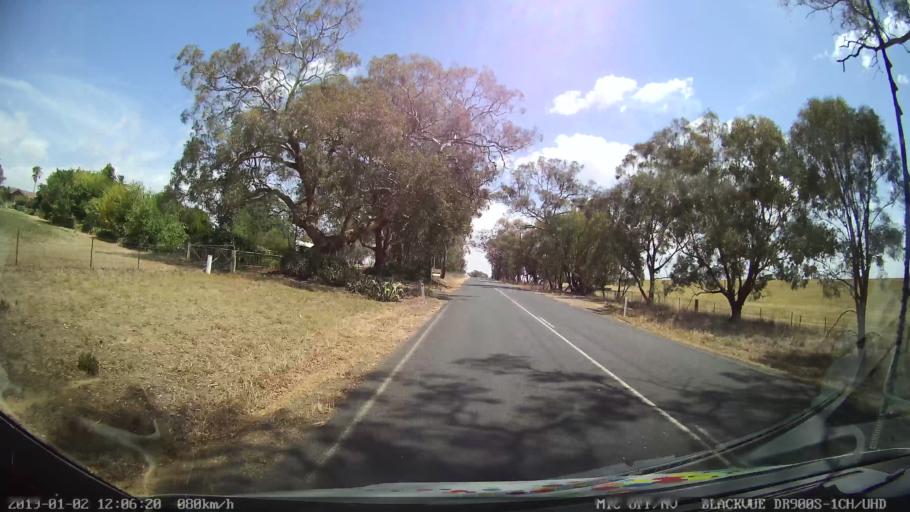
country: AU
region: New South Wales
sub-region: Young
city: Young
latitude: -34.5042
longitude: 148.2952
